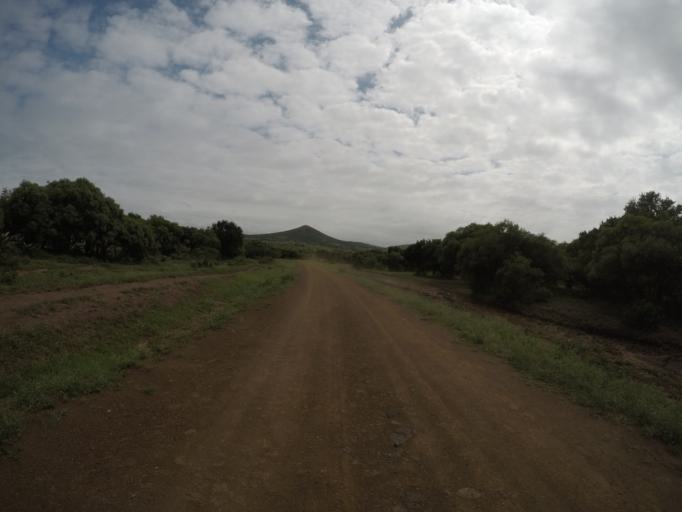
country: ZA
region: KwaZulu-Natal
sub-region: uThungulu District Municipality
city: Empangeni
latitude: -28.6219
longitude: 31.8559
